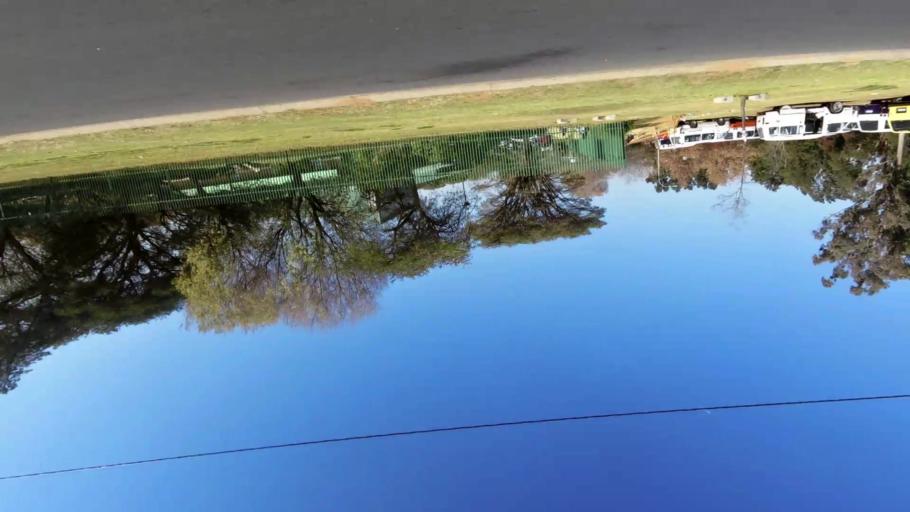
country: ZA
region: Gauteng
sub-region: City of Johannesburg Metropolitan Municipality
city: Johannesburg
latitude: -26.2433
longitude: 27.9982
